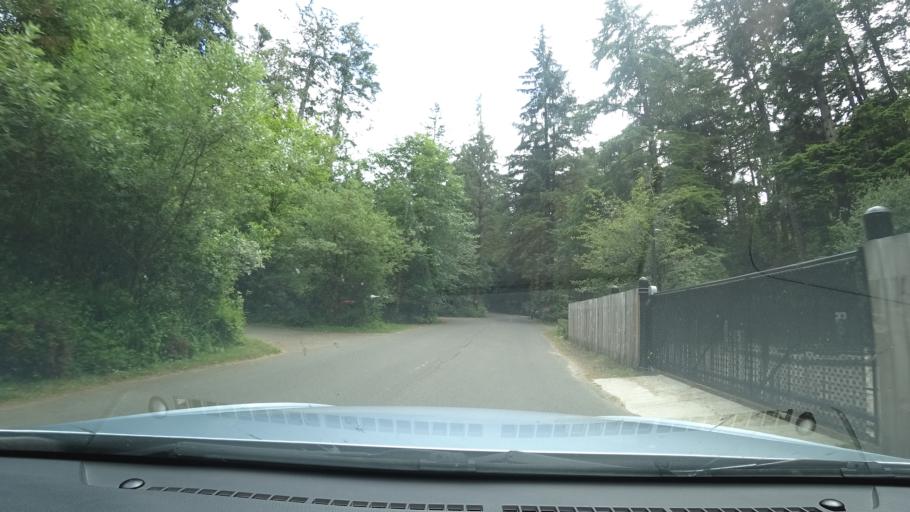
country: US
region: Oregon
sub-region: Lane County
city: Dunes City
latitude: 43.9250
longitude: -124.1119
